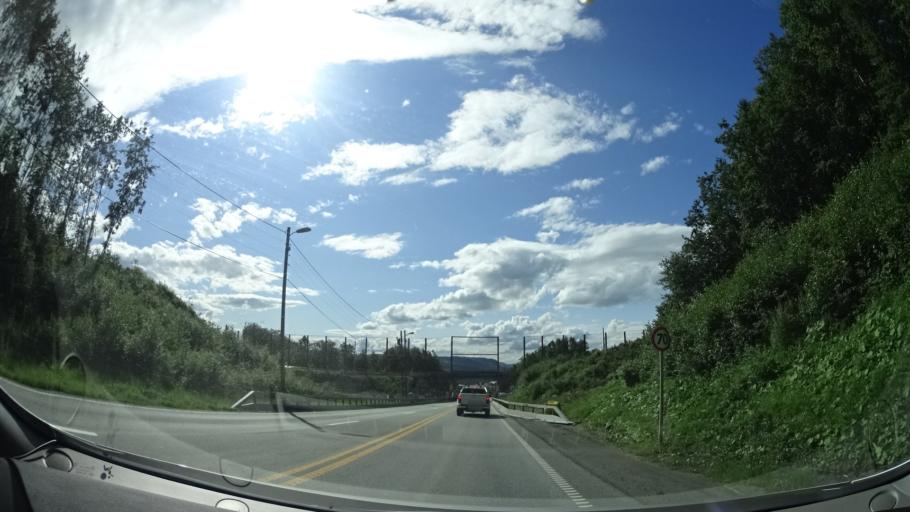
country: NO
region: Sor-Trondelag
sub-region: Melhus
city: Melhus
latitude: 63.3268
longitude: 10.3421
